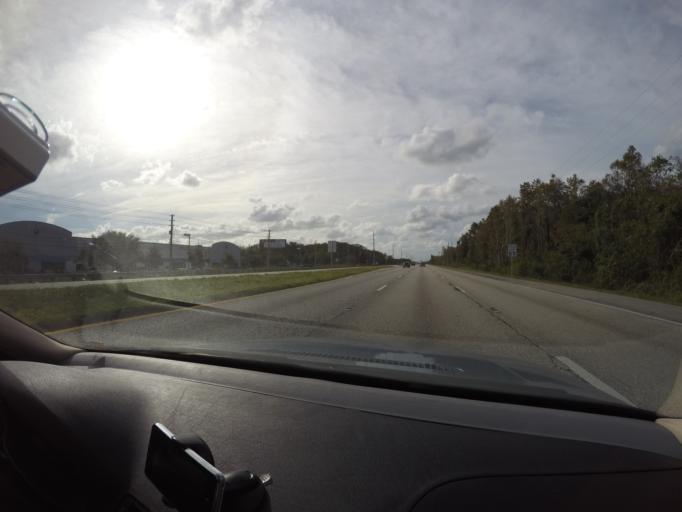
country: US
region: Florida
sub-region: Orange County
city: Belle Isle
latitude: 28.4511
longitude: -81.3747
